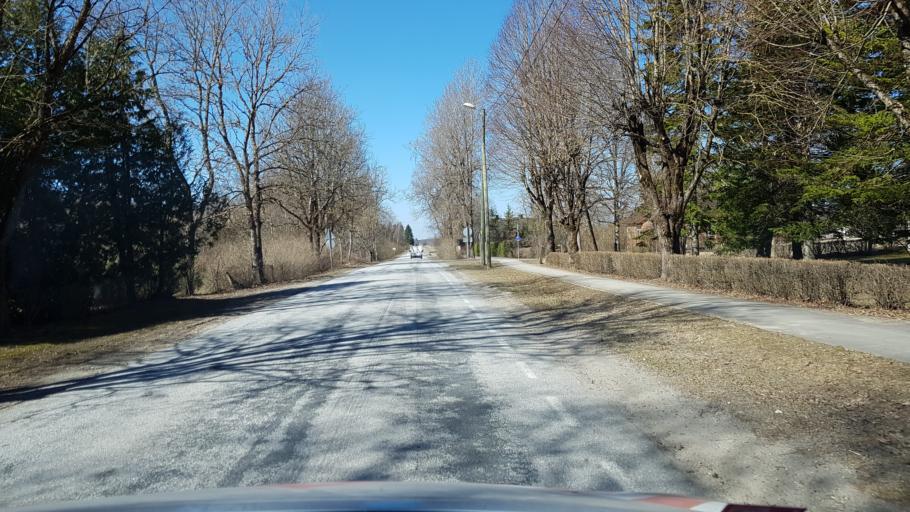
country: EE
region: Laeaene-Virumaa
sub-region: Rakke vald
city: Rakke
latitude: 58.9914
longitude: 26.2304
